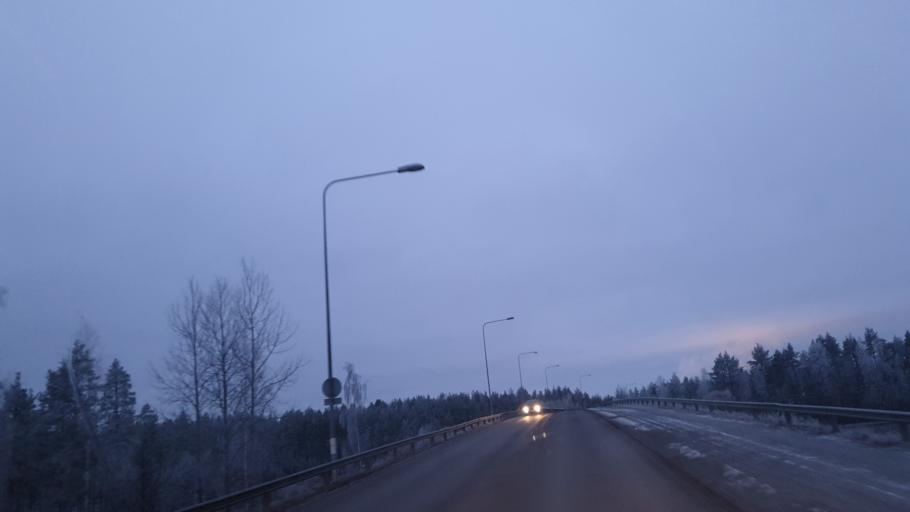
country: FI
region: Southern Ostrobothnia
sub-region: Seinaejoki
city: Nurmo
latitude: 62.7751
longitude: 22.8898
